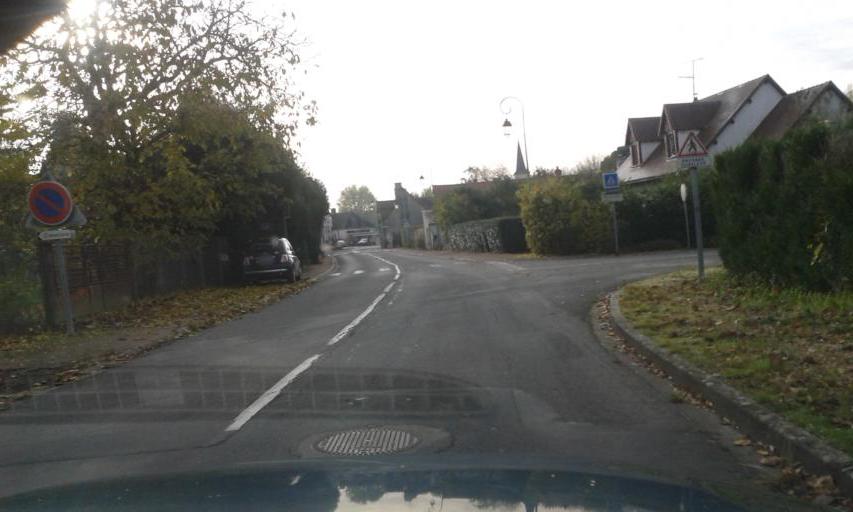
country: FR
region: Centre
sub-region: Departement du Loiret
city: Jouy-le-Potier
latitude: 47.7798
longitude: 1.8729
